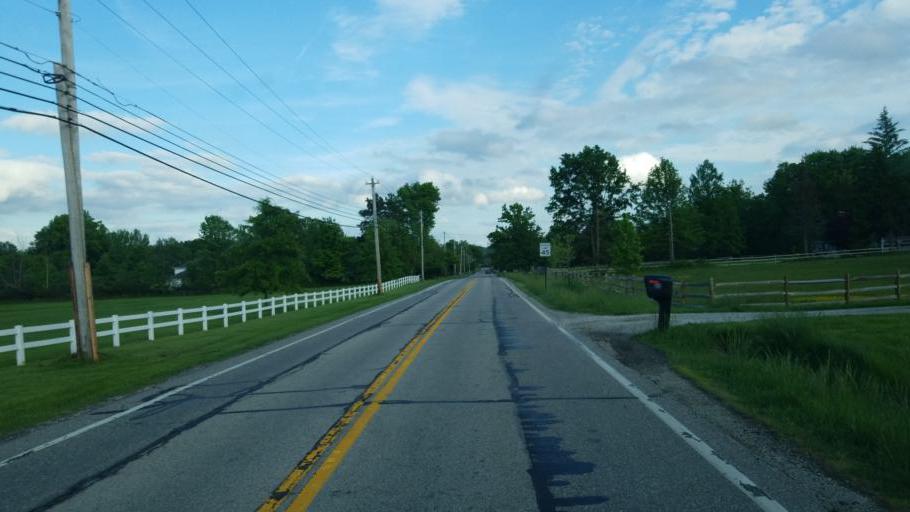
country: US
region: Ohio
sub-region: Summit County
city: Hudson
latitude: 41.2624
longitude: -81.4542
